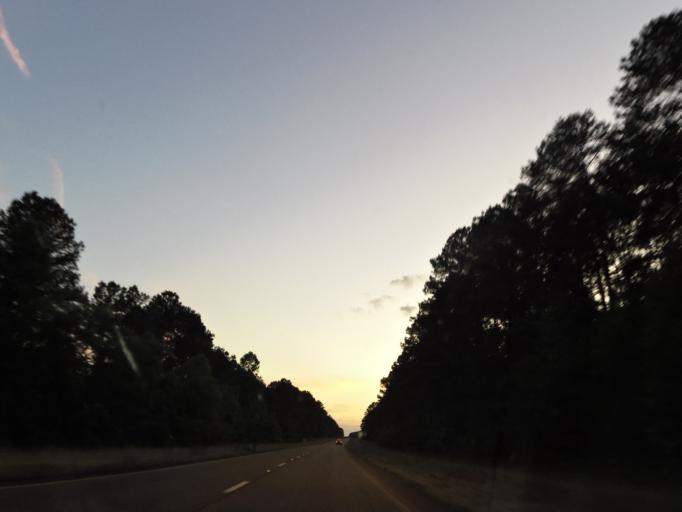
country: US
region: Mississippi
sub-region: Lauderdale County
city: Meridian Station
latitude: 32.5164
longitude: -88.5277
